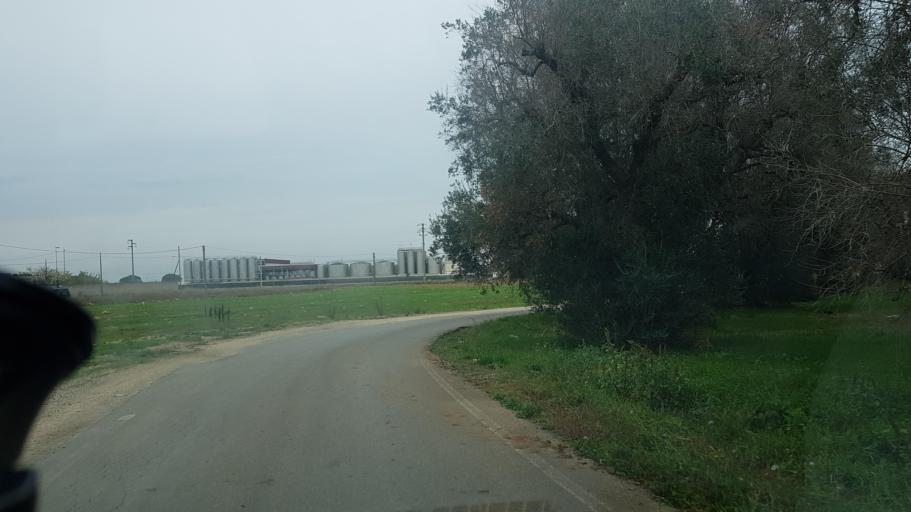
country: IT
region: Apulia
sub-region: Provincia di Brindisi
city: Cellino San Marco
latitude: 40.4775
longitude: 17.9675
